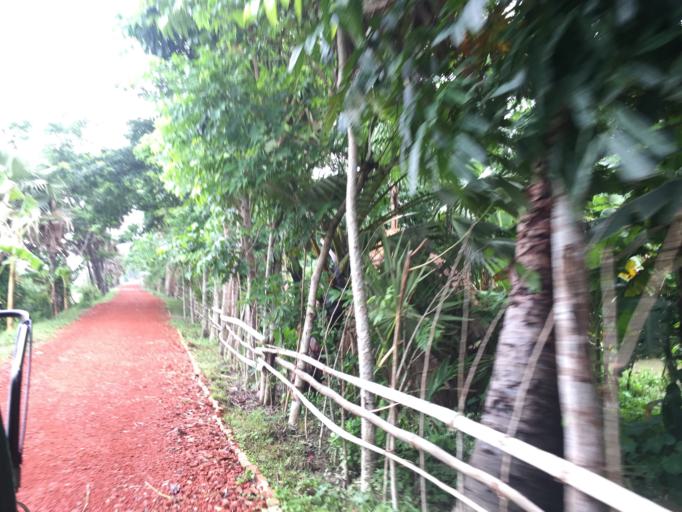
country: BD
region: Barisal
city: Mathba
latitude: 22.1954
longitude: 89.9334
